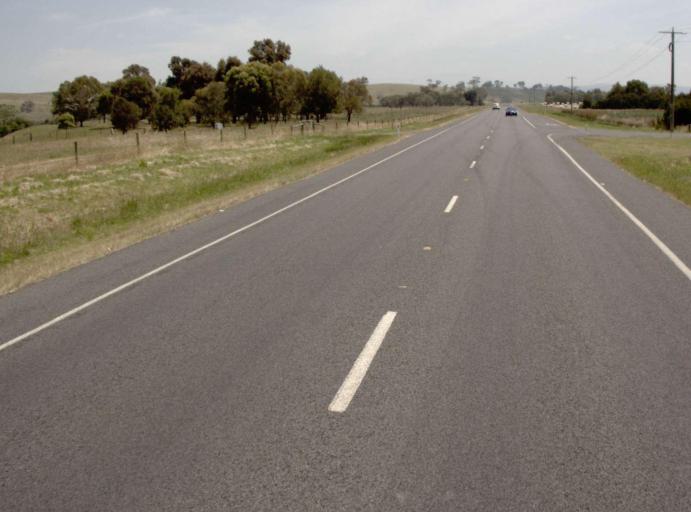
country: AU
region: Victoria
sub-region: Latrobe
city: Traralgon
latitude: -38.2392
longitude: 146.5437
